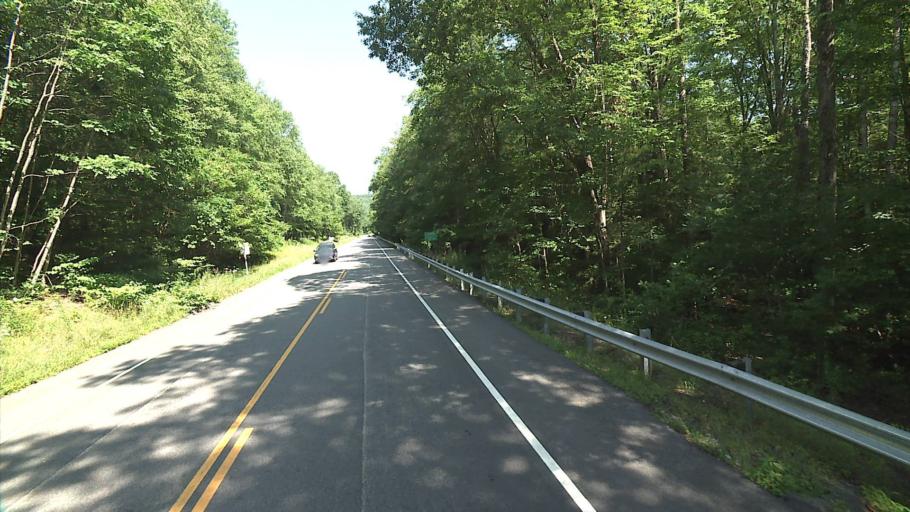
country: US
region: Connecticut
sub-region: Litchfield County
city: Winchester Center
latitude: 41.8862
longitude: -73.1730
